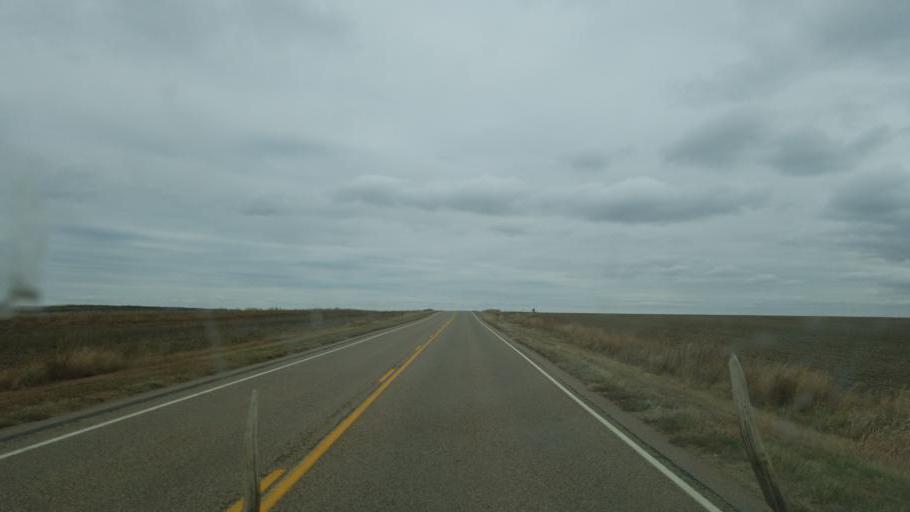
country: US
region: Colorado
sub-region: Cheyenne County
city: Cheyenne Wells
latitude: 38.8454
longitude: -102.2513
